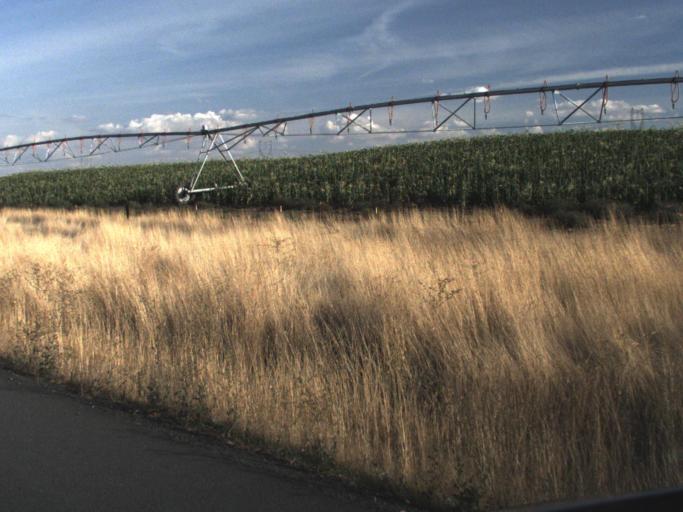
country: US
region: Oregon
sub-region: Umatilla County
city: Umatilla
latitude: 45.9477
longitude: -119.3844
